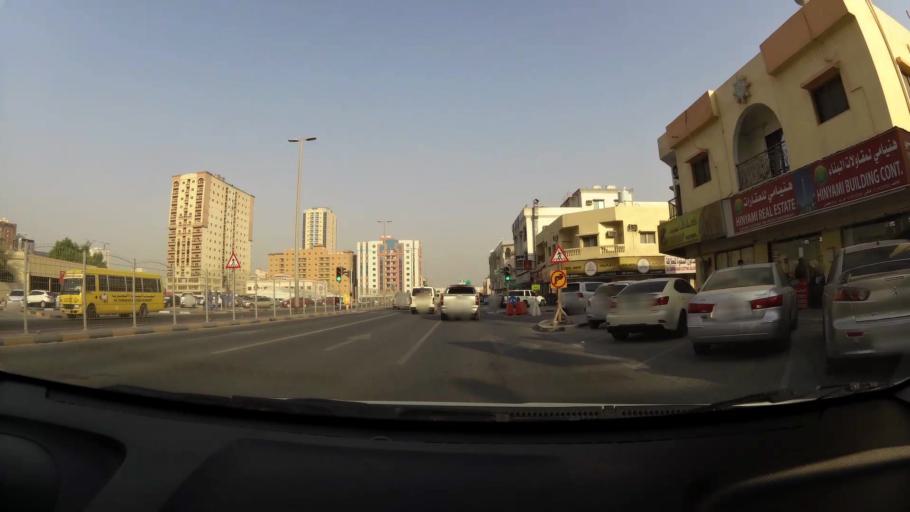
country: AE
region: Ajman
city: Ajman
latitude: 25.3850
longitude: 55.4610
